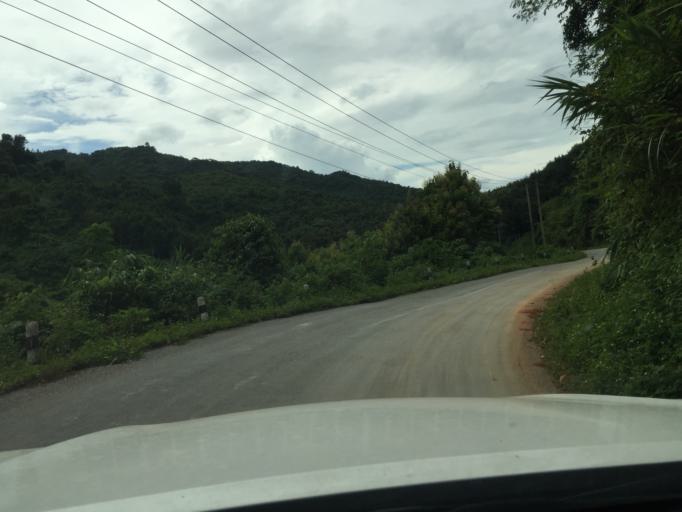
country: LA
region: Oudomxai
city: Muang La
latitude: 21.1028
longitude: 102.2207
